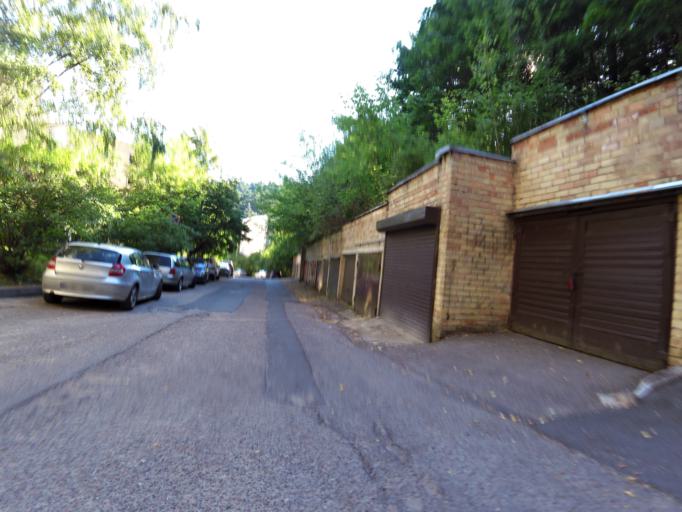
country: LT
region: Vilnius County
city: Rasos
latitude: 54.7025
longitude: 25.3200
